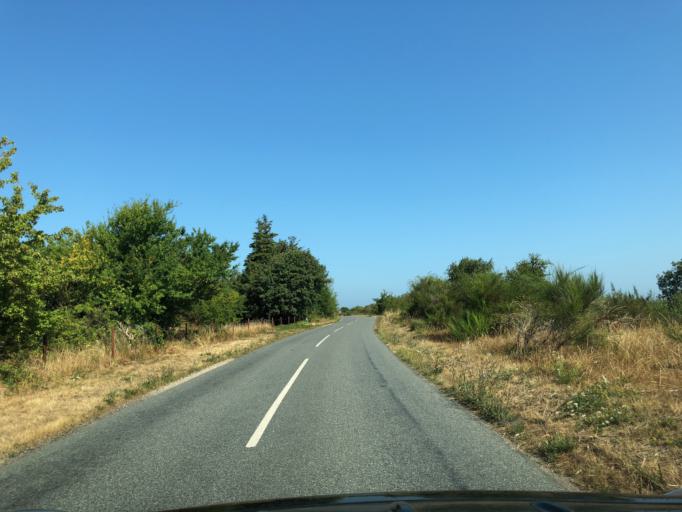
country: DK
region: Zealand
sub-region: Odsherred Kommune
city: Asnaes
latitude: 55.9951
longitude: 11.2906
